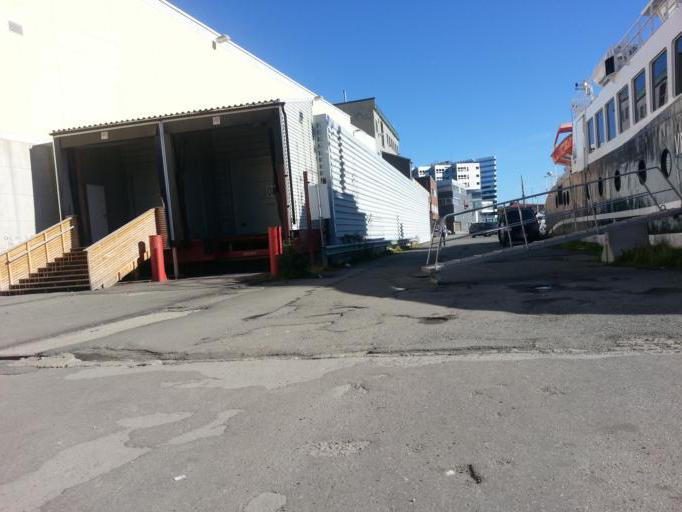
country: NO
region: Troms
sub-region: Tromso
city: Tromso
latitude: 69.6448
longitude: 18.9520
